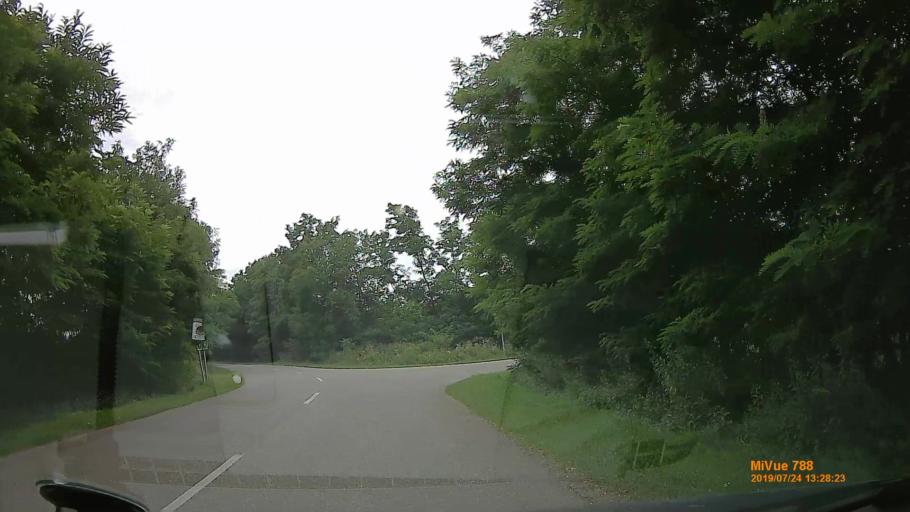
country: UA
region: Zakarpattia
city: Batiovo
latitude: 48.2232
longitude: 22.4163
